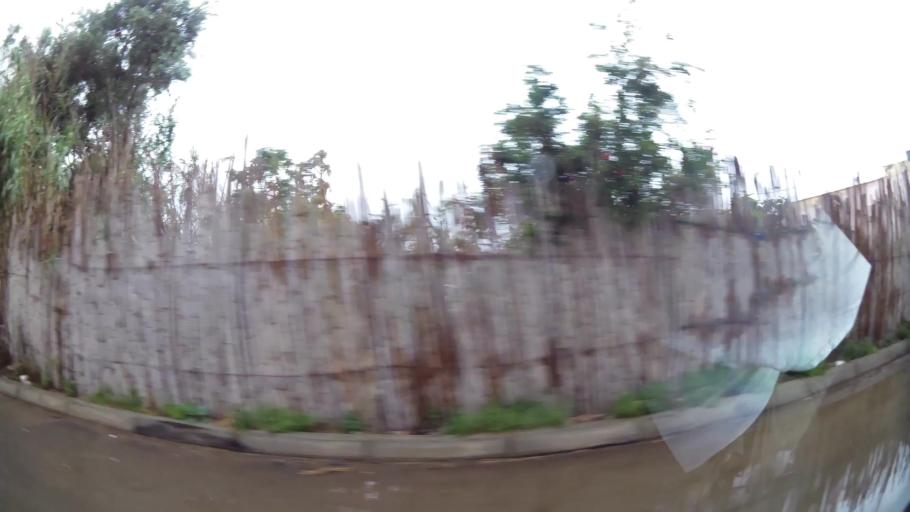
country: MA
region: Oriental
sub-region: Nador
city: Nador
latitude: 35.1568
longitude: -2.9516
